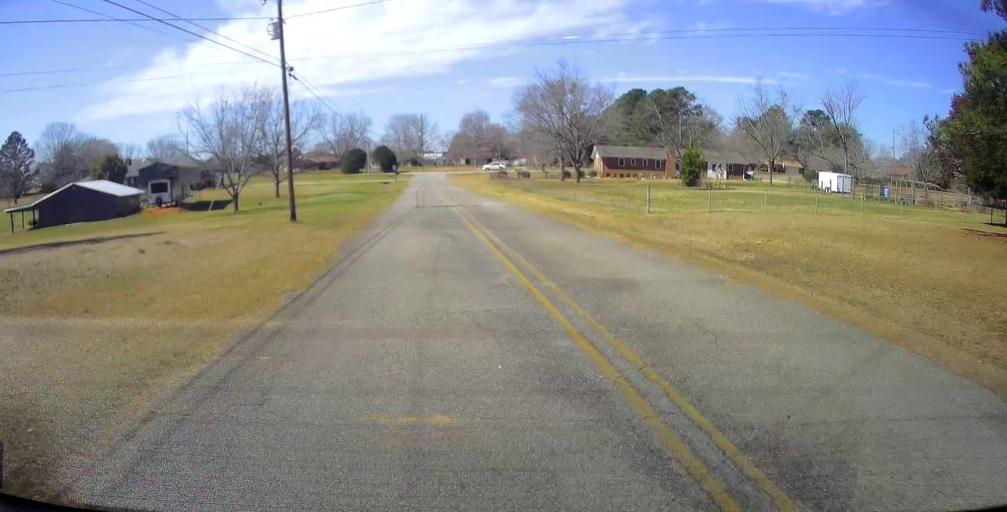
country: US
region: Georgia
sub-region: Houston County
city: Warner Robins
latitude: 32.5645
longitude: -83.6364
